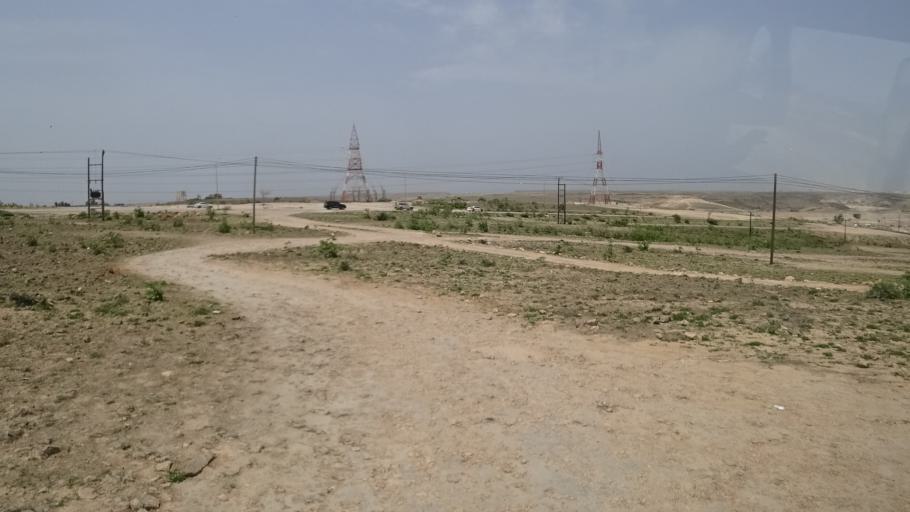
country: OM
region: Zufar
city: Salalah
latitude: 17.0659
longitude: 54.4364
